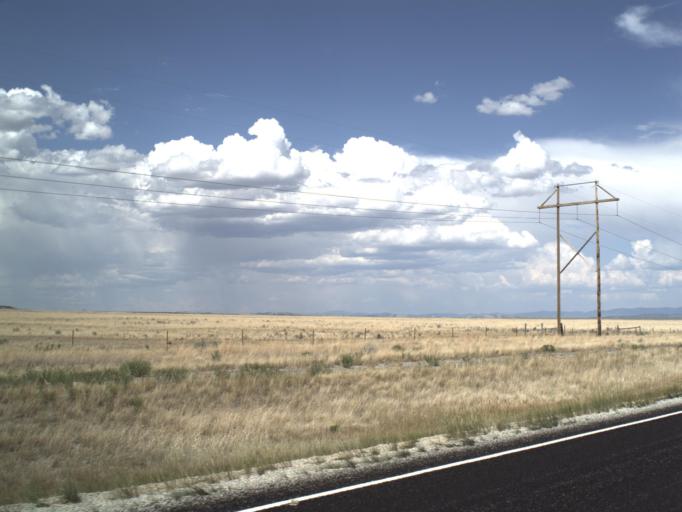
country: US
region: Idaho
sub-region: Power County
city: American Falls
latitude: 41.9687
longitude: -113.1030
